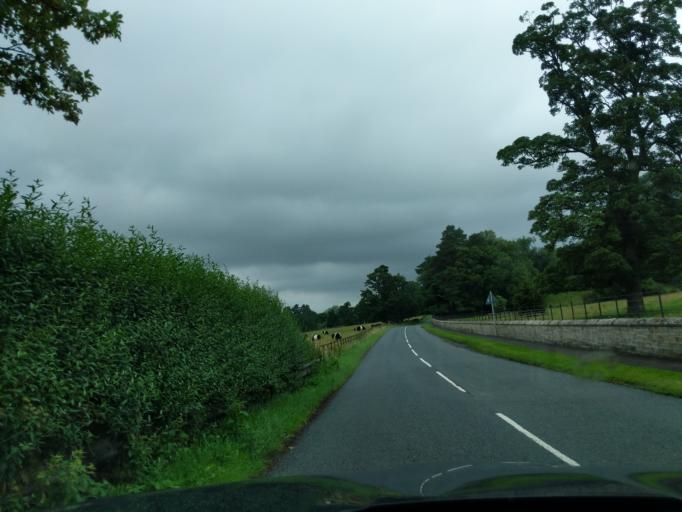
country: GB
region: England
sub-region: Northumberland
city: Ford
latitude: 55.6285
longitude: -2.0939
